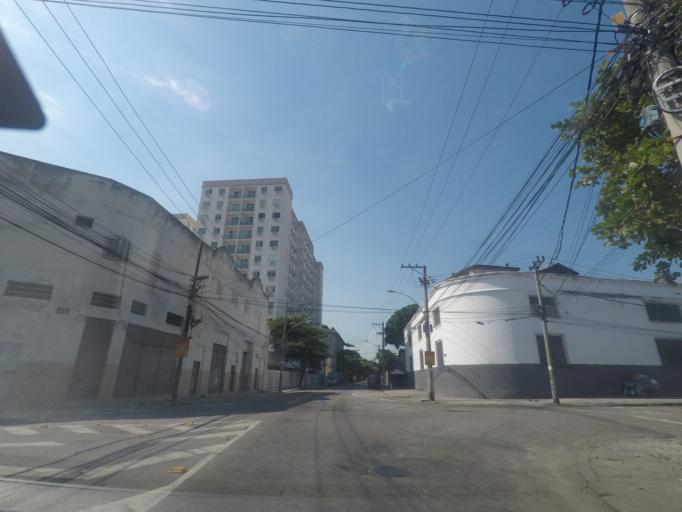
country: BR
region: Rio de Janeiro
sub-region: Rio De Janeiro
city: Rio de Janeiro
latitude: -22.8937
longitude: -43.2185
